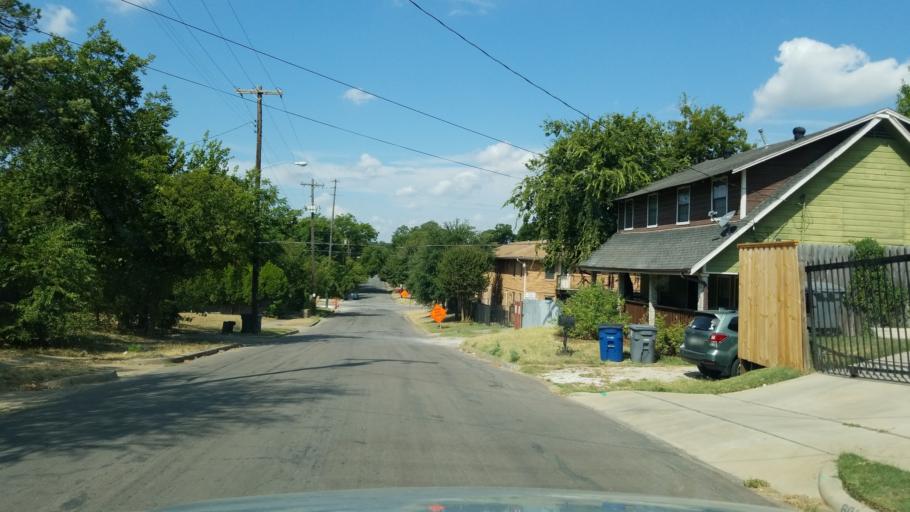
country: US
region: Texas
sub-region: Dallas County
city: Dallas
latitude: 32.7548
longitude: -96.8145
